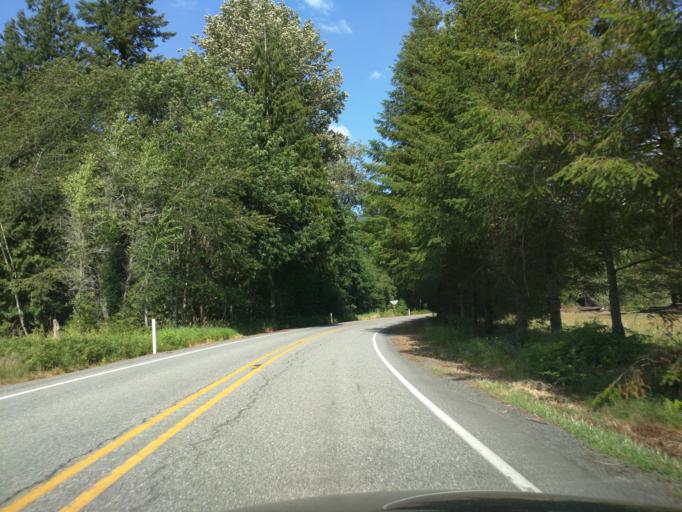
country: US
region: Washington
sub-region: Whatcom County
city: Peaceful Valley
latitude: 48.9276
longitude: -122.0479
